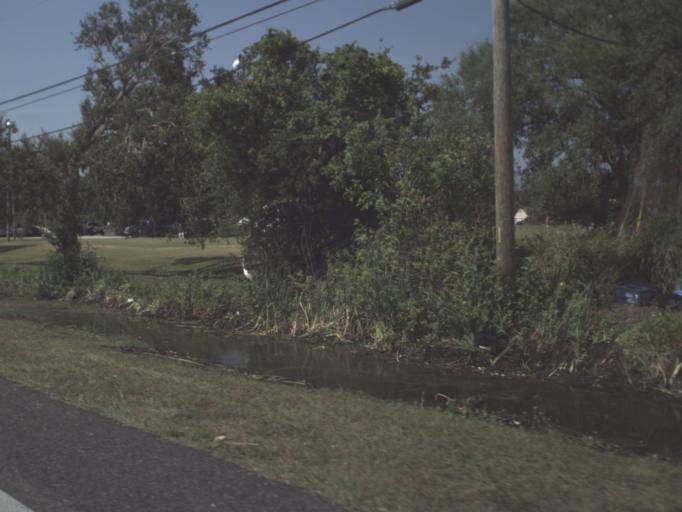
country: US
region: Florida
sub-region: Brevard County
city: Rockledge
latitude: 28.2744
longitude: -80.6927
